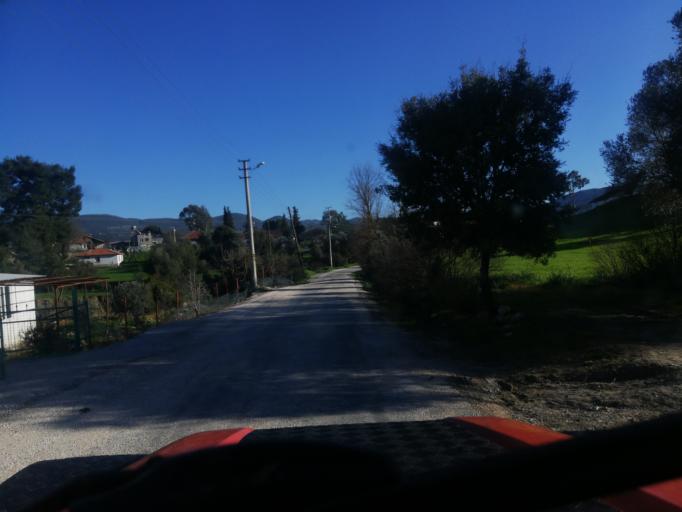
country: TR
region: Antalya
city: Kas
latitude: 36.2900
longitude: 29.7064
